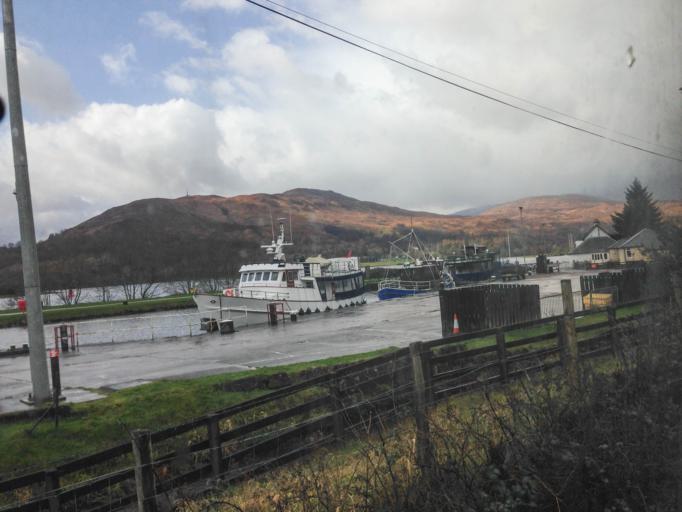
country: GB
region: Scotland
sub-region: Highland
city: Fort William
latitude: 56.8427
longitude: -5.1212
